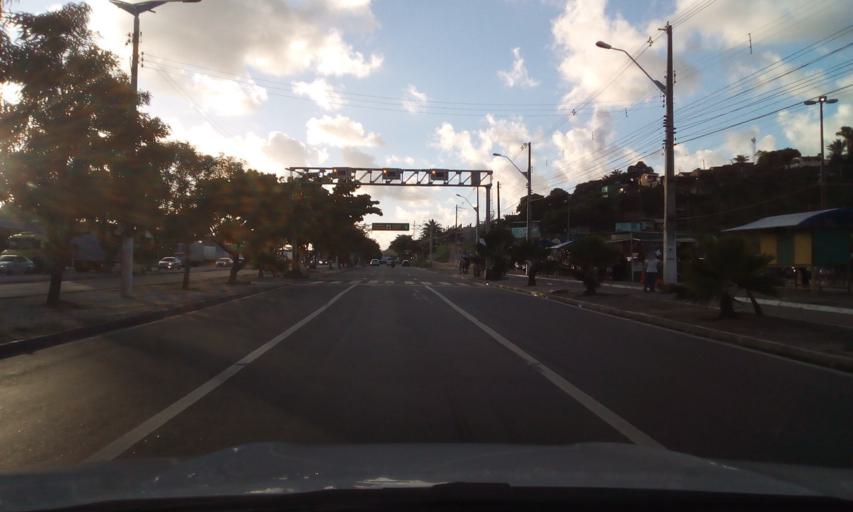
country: BR
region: Pernambuco
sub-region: Abreu E Lima
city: Abreu e Lima
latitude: -7.9144
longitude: -34.8988
